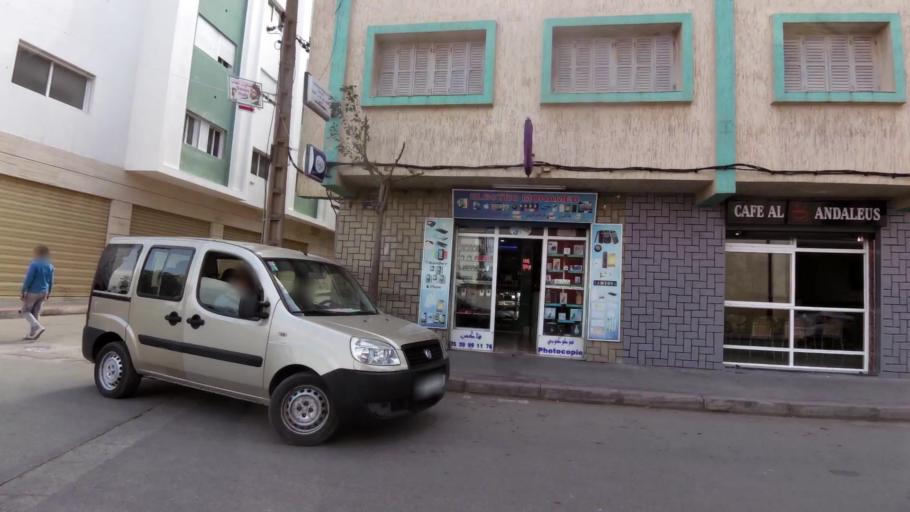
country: MA
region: Tanger-Tetouan
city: Tetouan
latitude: 35.5868
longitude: -5.3496
